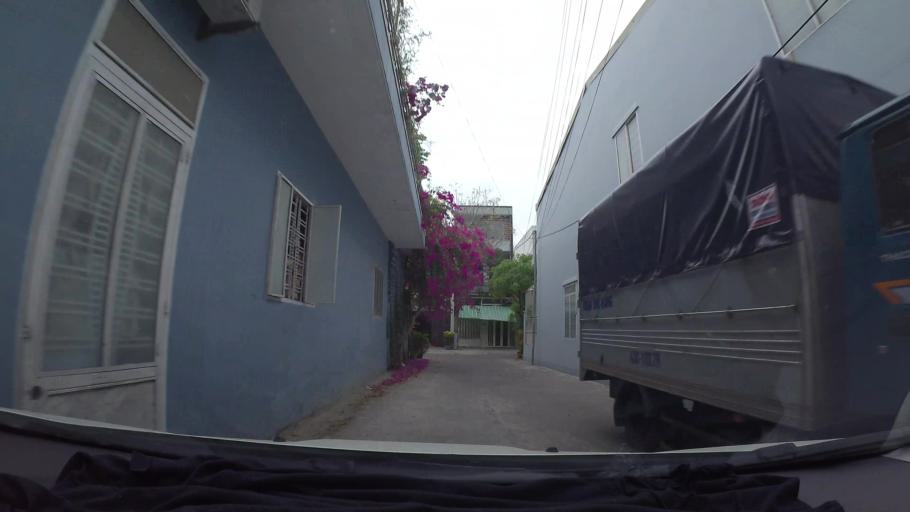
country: VN
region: Da Nang
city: Thanh Khe
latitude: 16.0545
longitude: 108.1761
